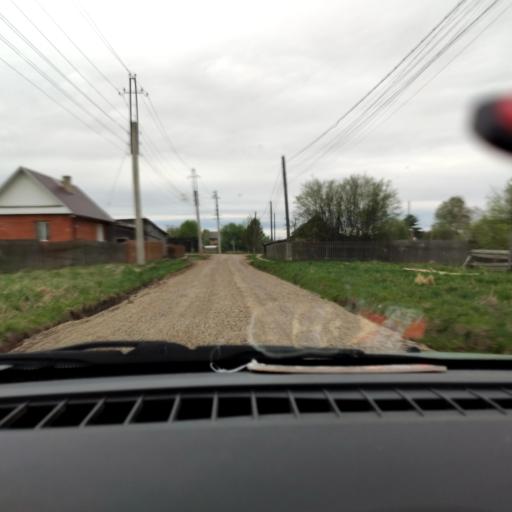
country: RU
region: Perm
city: Kudymkar
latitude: 59.0136
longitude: 54.6243
